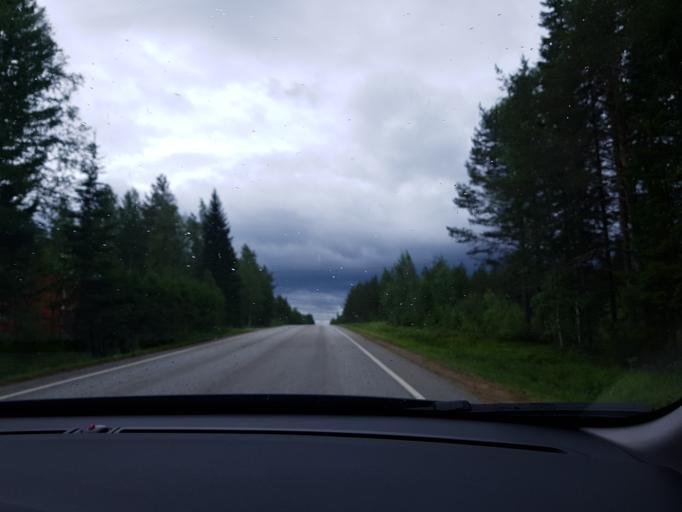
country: FI
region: Kainuu
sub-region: Kehys-Kainuu
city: Kuhmo
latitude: 64.1583
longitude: 29.4644
